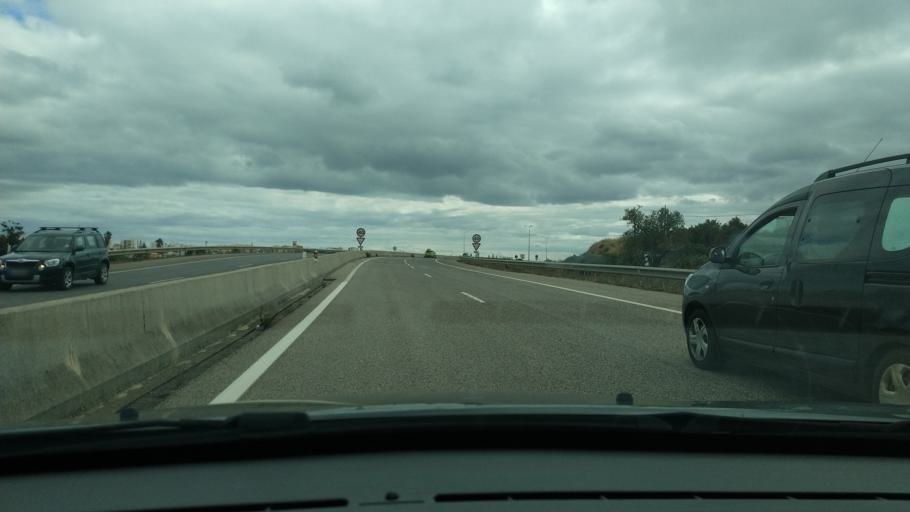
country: PT
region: Faro
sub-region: Lagos
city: Lagos
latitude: 37.1039
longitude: -8.6955
